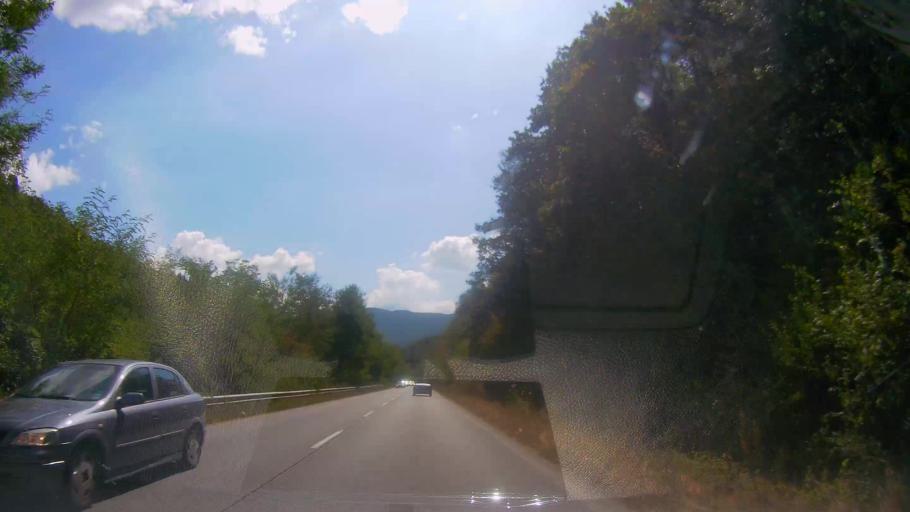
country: BG
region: Stara Zagora
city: Gurkovo
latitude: 42.7300
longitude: 25.7121
